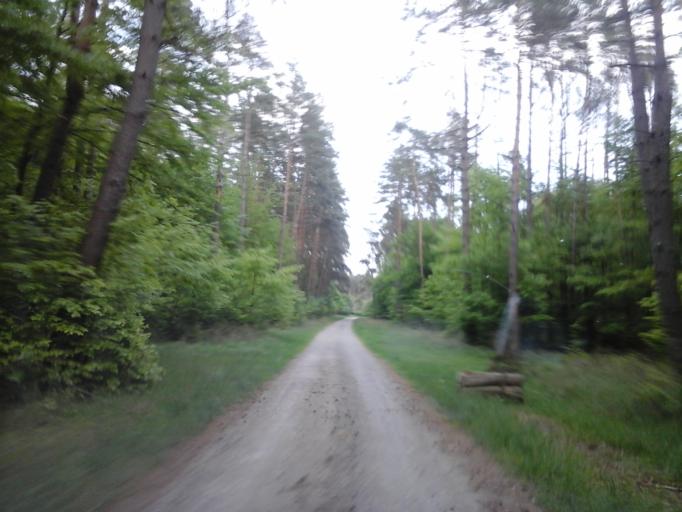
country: PL
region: West Pomeranian Voivodeship
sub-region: Powiat choszczenski
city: Pelczyce
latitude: 52.9482
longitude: 15.3436
